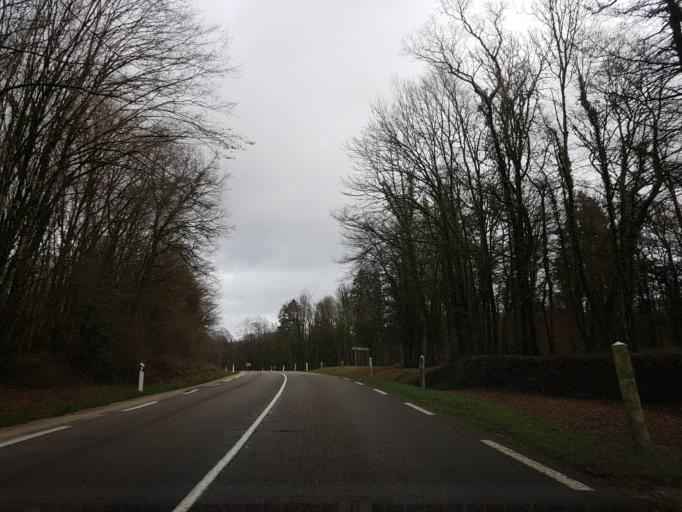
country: FR
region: Franche-Comte
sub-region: Departement de la Haute-Saone
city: Scey-sur-Saone-et-Saint-Albin
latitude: 47.6882
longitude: 5.9999
